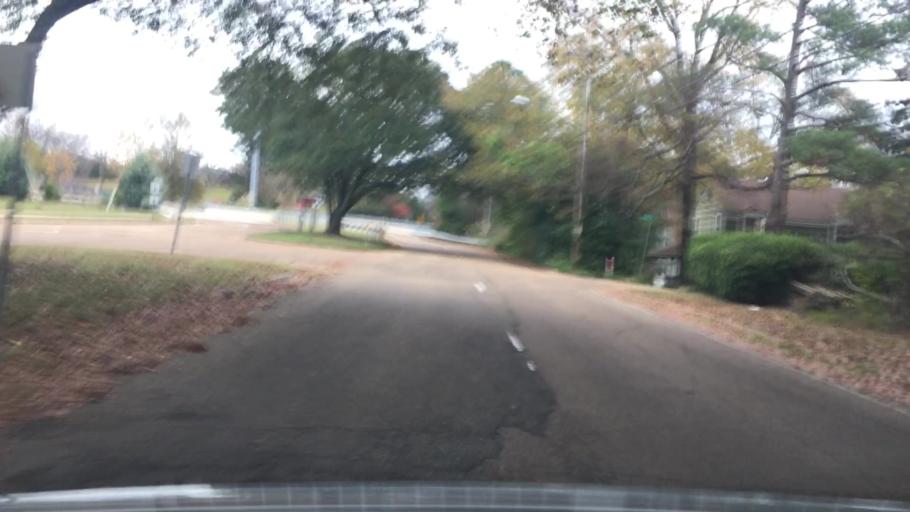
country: US
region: Mississippi
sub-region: Rankin County
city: Flowood
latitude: 32.3233
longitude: -90.1601
